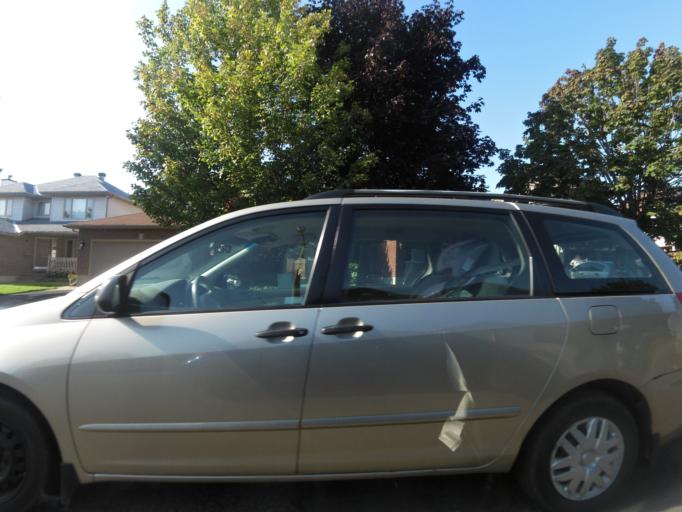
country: CA
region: Ontario
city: Clarence-Rockland
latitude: 45.4808
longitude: -75.4822
